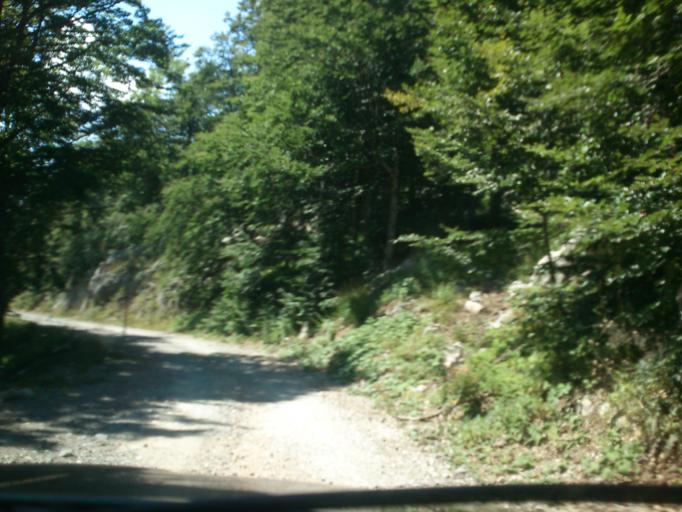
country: HR
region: Licko-Senjska
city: Senj
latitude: 44.8208
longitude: 14.9875
